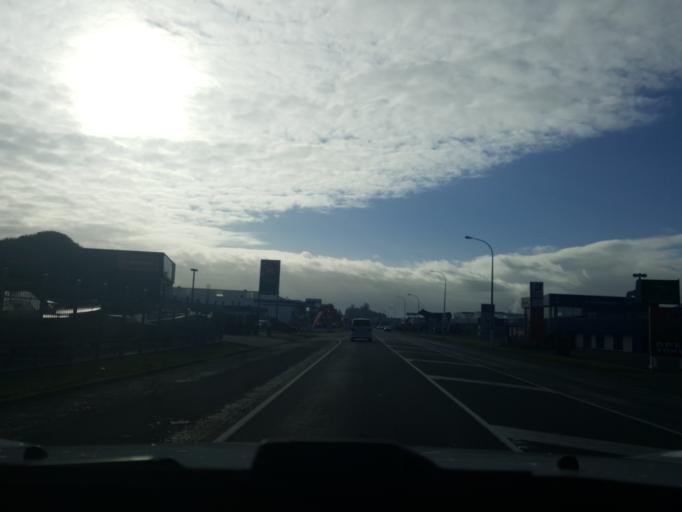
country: NZ
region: Waikato
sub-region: Waipa District
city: Cambridge
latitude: -37.6609
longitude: 175.5200
